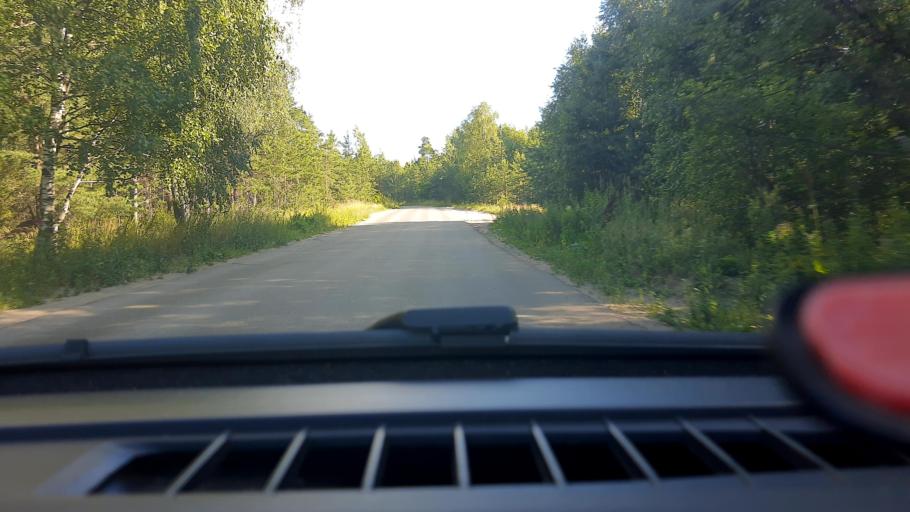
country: RU
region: Nizjnij Novgorod
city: Babino
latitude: 56.3102
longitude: 43.6301
